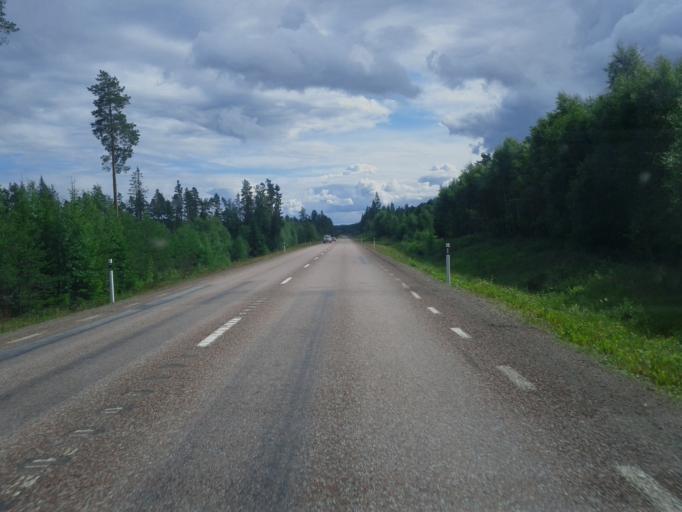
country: SE
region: Dalarna
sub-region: Rattviks Kommun
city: Raettvik
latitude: 60.8156
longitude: 15.2592
